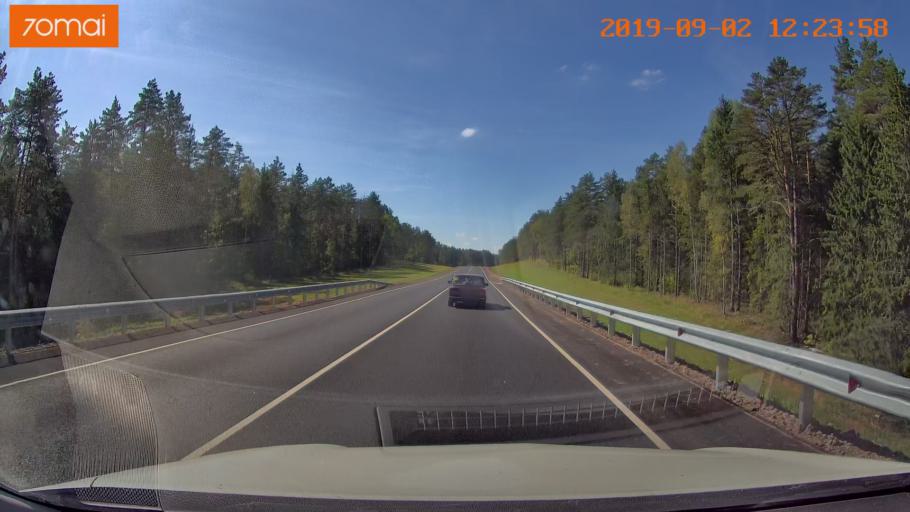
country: RU
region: Smolensk
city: Shumyachi
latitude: 53.8720
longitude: 32.6155
